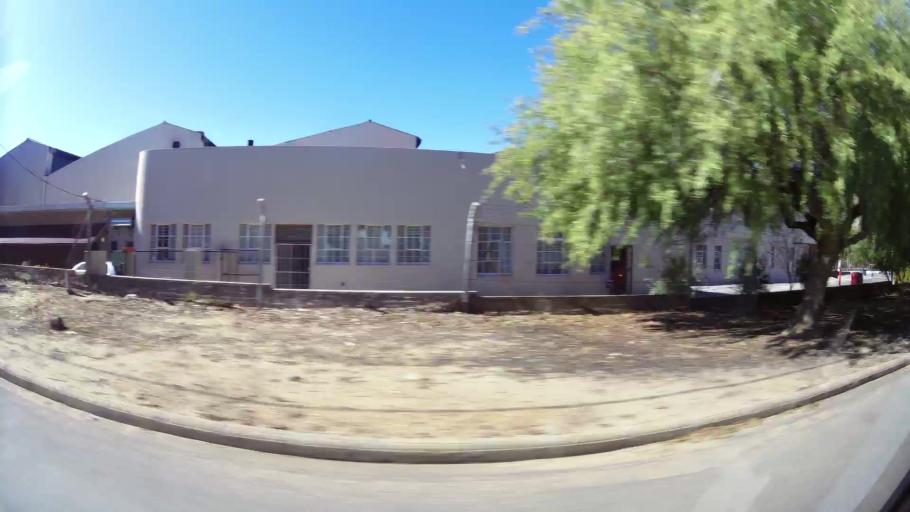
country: ZA
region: Western Cape
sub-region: Cape Winelands District Municipality
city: Ashton
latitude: -33.7826
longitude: 20.1302
